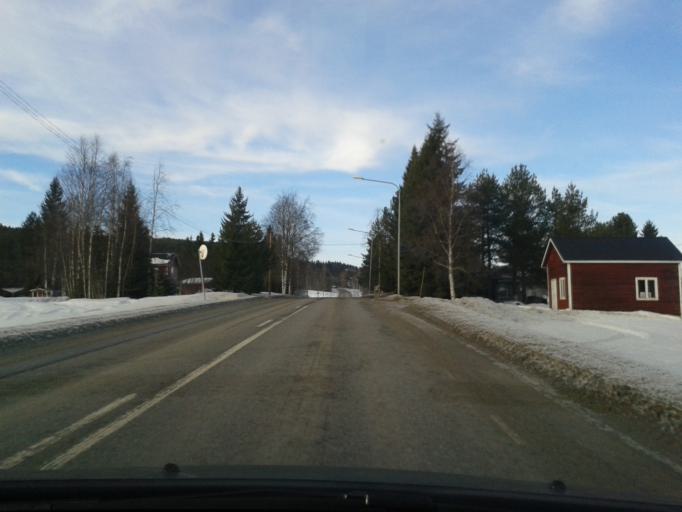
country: SE
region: Vaesternorrland
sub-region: OErnskoeldsviks Kommun
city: Bredbyn
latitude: 63.4845
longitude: 18.0876
